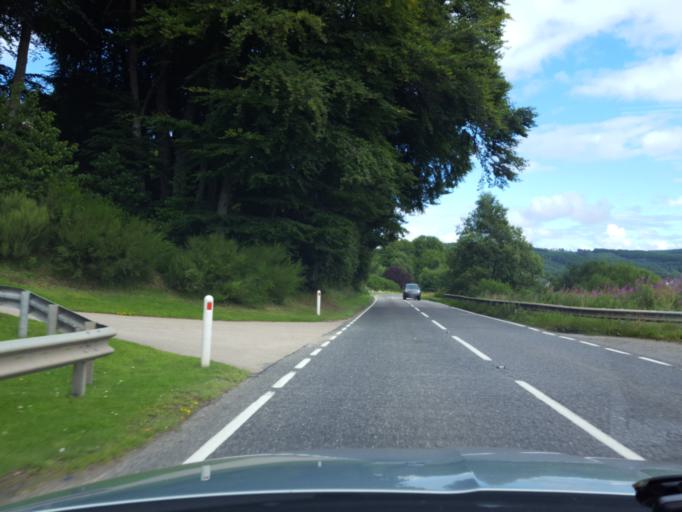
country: GB
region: Scotland
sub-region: Moray
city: Rothes
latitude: 57.5185
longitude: -3.2092
